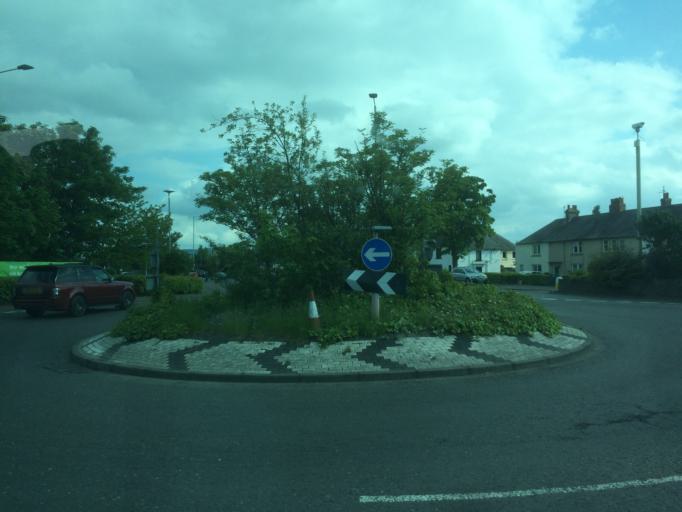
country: GB
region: Scotland
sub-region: Perth and Kinross
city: Perth
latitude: 56.4064
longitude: -3.4462
